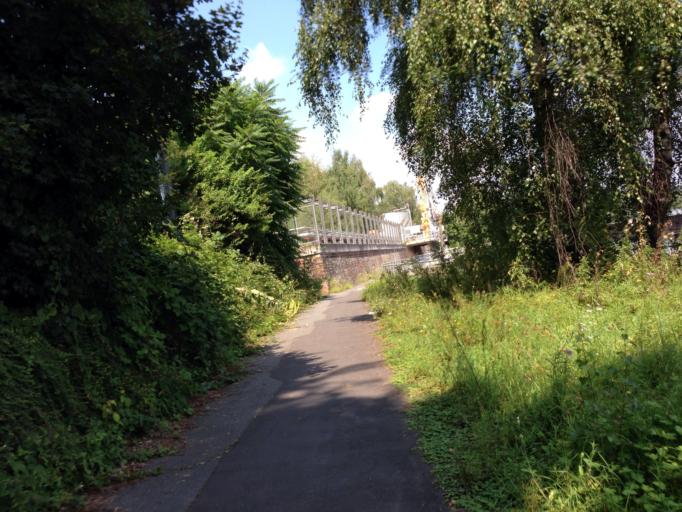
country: DE
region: Hesse
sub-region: Regierungsbezirk Darmstadt
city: Offenbach
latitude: 50.1312
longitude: 8.7678
